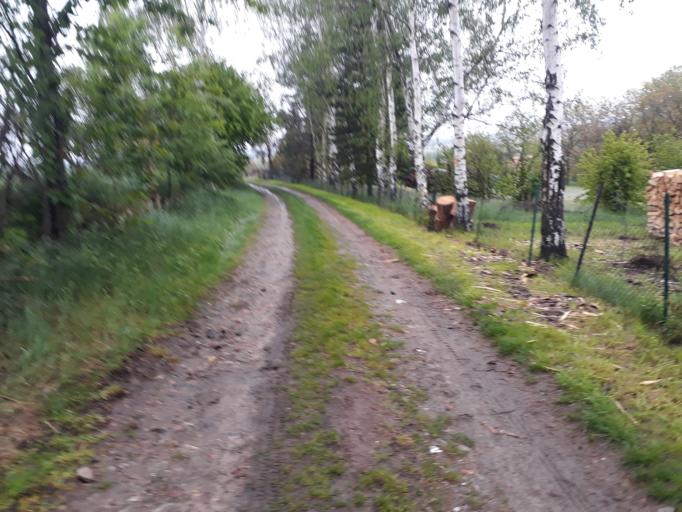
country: DE
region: Saxony
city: Reinhardtsgrimma
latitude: 50.8919
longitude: 13.7443
